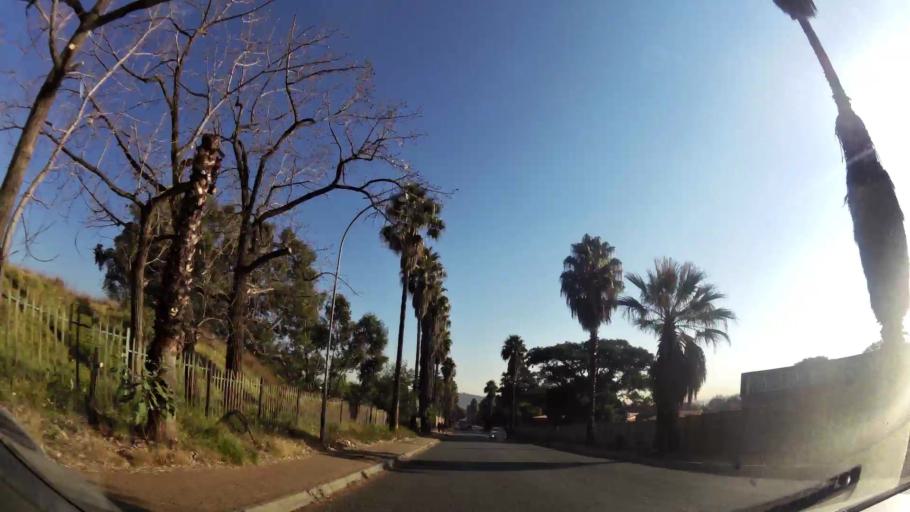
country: ZA
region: Gauteng
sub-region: Ekurhuleni Metropolitan Municipality
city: Germiston
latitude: -26.1932
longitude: 28.1288
